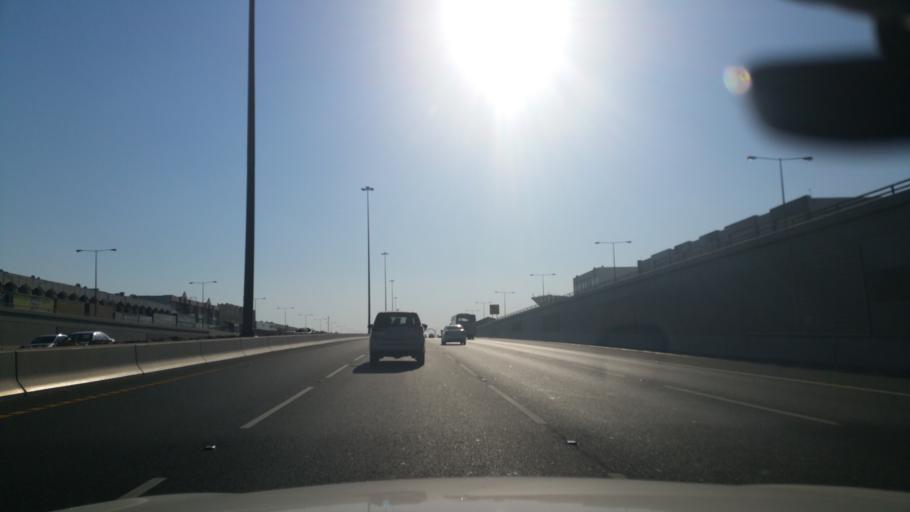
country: QA
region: Baladiyat ar Rayyan
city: Ar Rayyan
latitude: 25.2324
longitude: 51.4431
